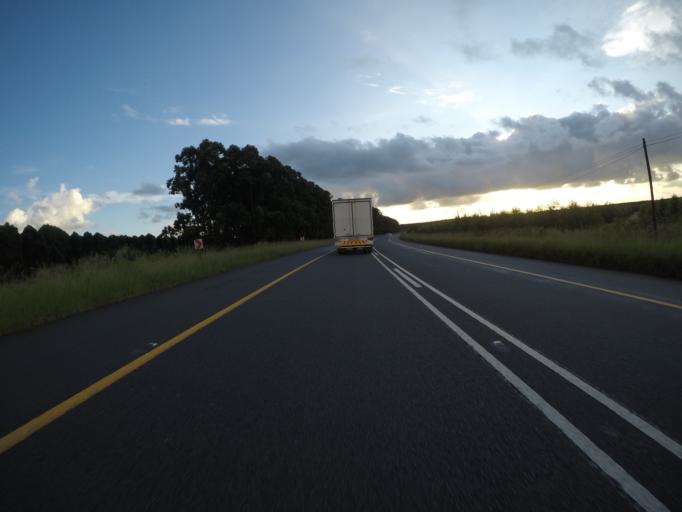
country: ZA
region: KwaZulu-Natal
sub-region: uThungulu District Municipality
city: KwaMbonambi
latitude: -28.5766
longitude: 32.1053
